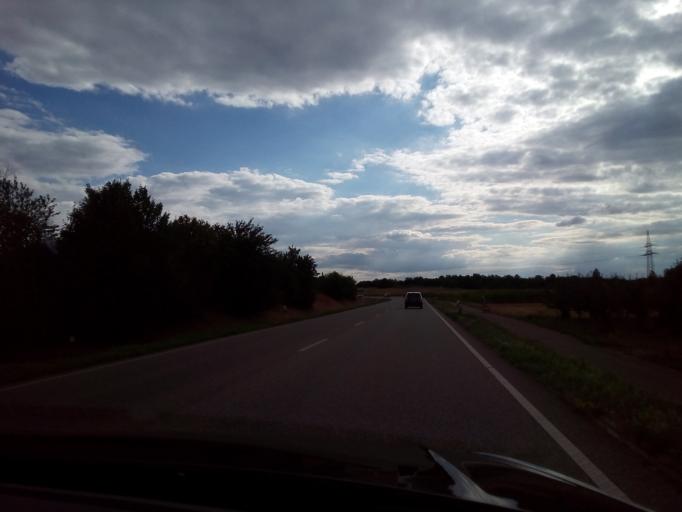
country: DE
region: Baden-Wuerttemberg
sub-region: Freiburg Region
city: Renchen
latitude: 48.5706
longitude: 7.9902
